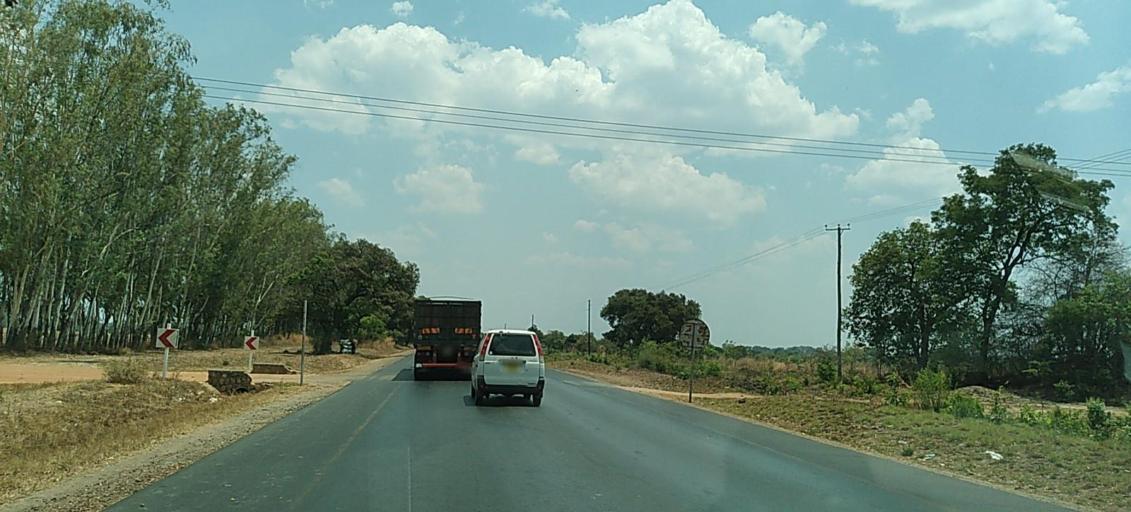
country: ZM
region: Central
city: Kabwe
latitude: -14.2342
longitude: 28.5706
